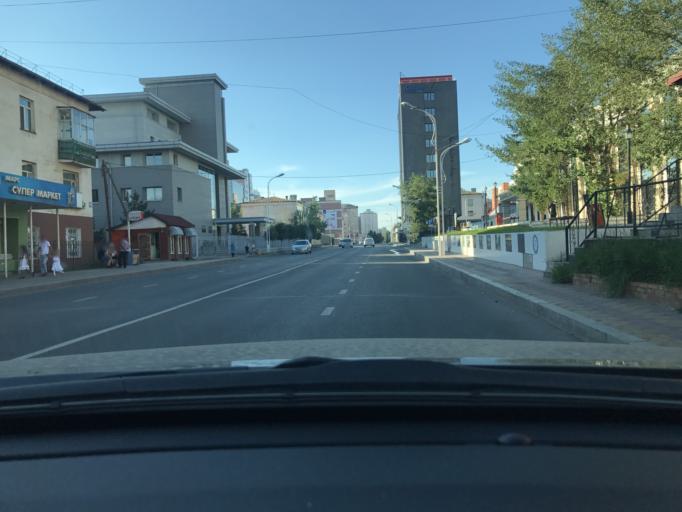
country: MN
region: Ulaanbaatar
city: Ulaanbaatar
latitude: 47.9193
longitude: 106.9353
